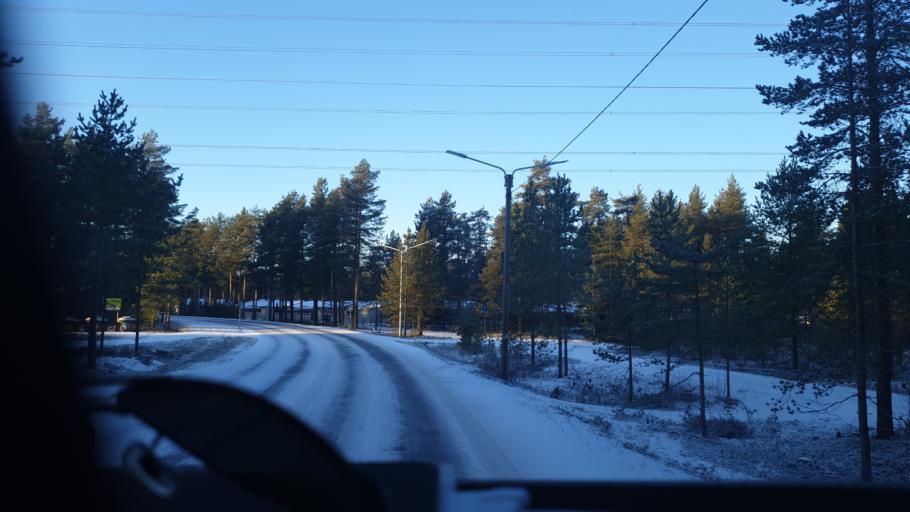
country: FI
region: Central Ostrobothnia
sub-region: Kokkola
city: Kokkola
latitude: 63.8256
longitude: 23.0899
